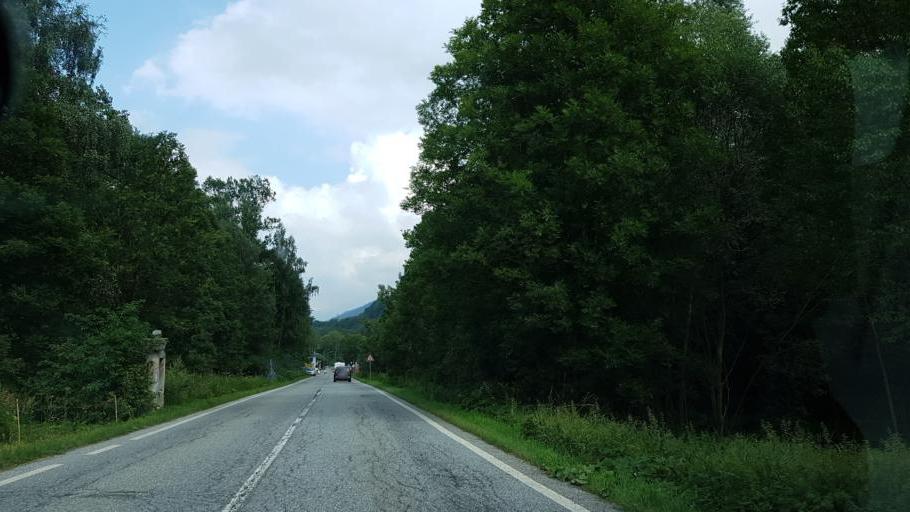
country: IT
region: Piedmont
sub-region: Provincia di Cuneo
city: Sampeyre
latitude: 44.5804
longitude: 7.1522
